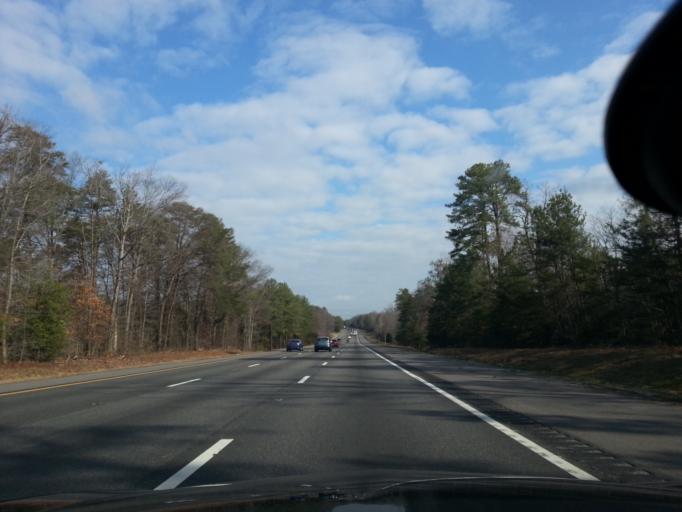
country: US
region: Virginia
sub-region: Caroline County
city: Bowling Green
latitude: 38.0379
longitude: -77.4991
